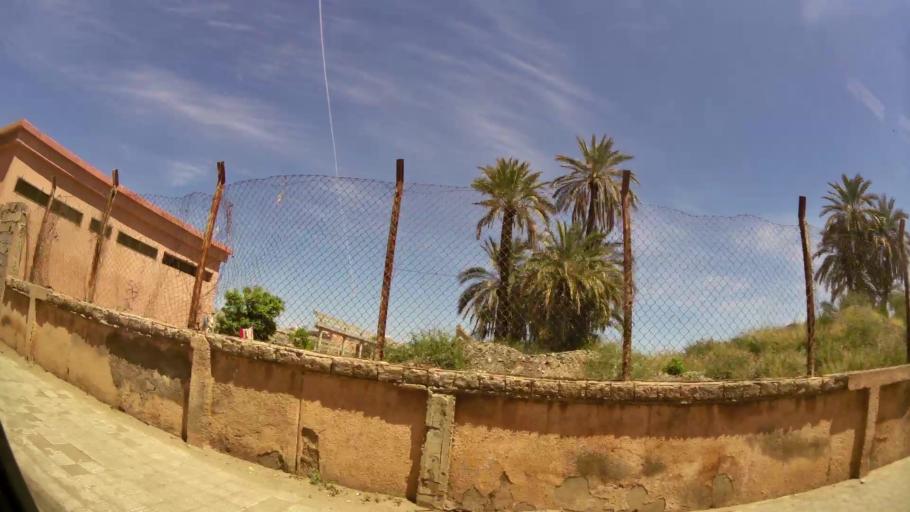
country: MA
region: Marrakech-Tensift-Al Haouz
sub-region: Marrakech
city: Marrakesh
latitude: 31.6536
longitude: -7.9976
